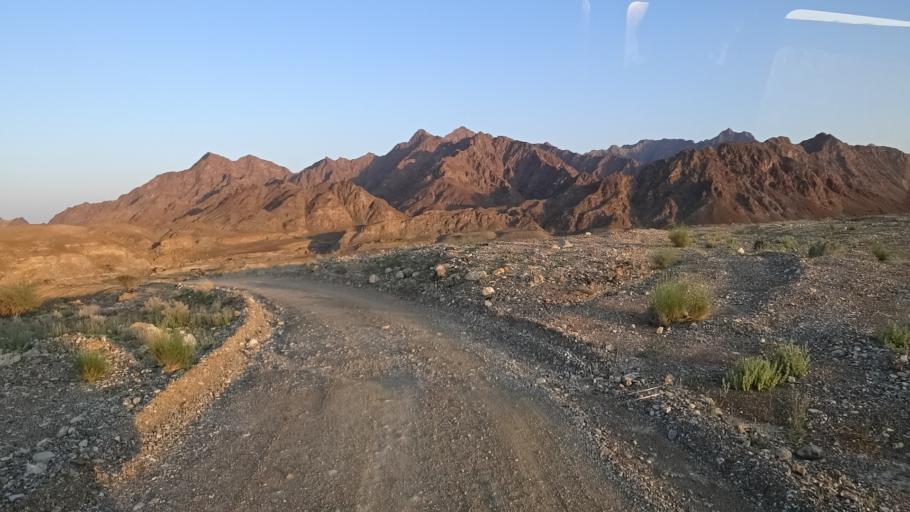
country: OM
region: Al Batinah
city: Al Khaburah
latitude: 23.7502
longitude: 56.9251
